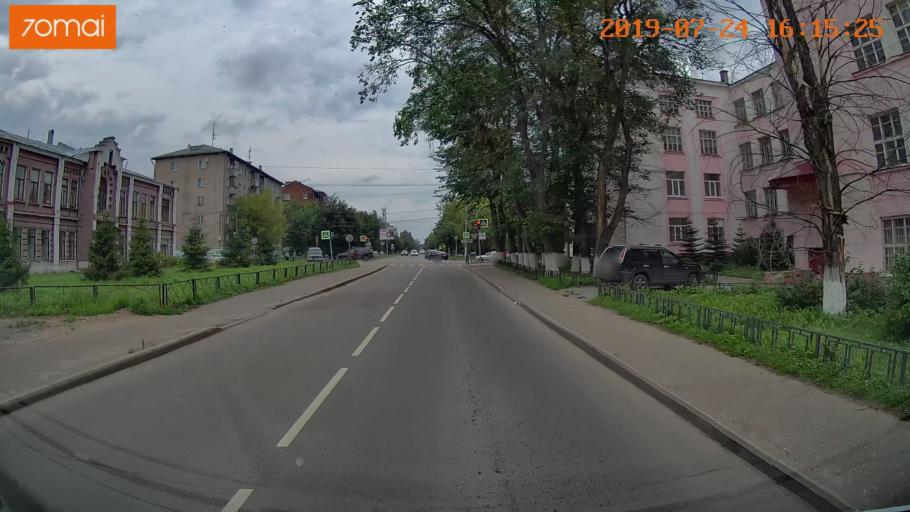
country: RU
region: Ivanovo
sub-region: Gorod Ivanovo
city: Ivanovo
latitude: 57.0053
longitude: 40.9804
